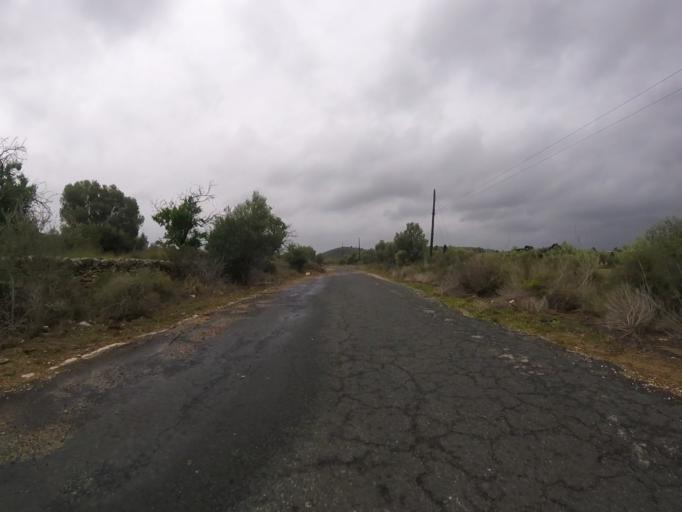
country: ES
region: Valencia
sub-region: Provincia de Castello
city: Alcala de Xivert
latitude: 40.2811
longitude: 0.2251
